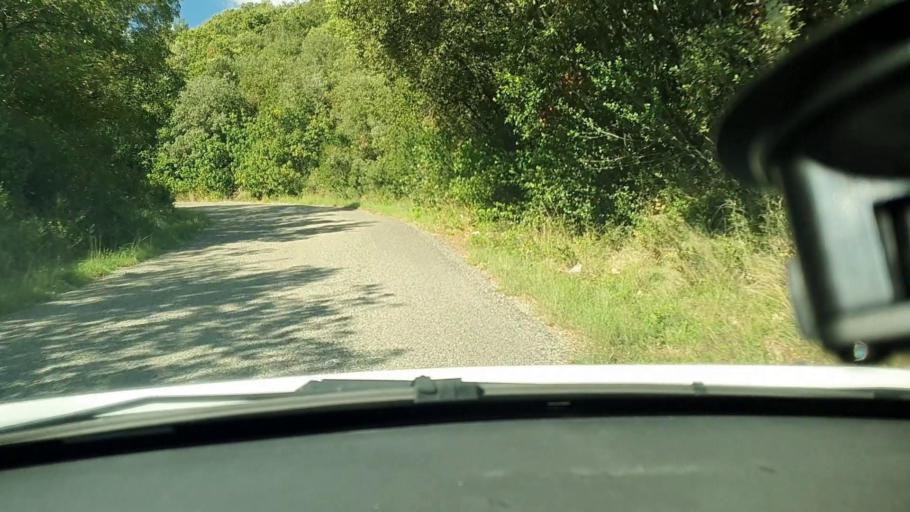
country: FR
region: Languedoc-Roussillon
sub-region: Departement du Gard
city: Goudargues
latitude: 44.1580
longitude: 4.4250
